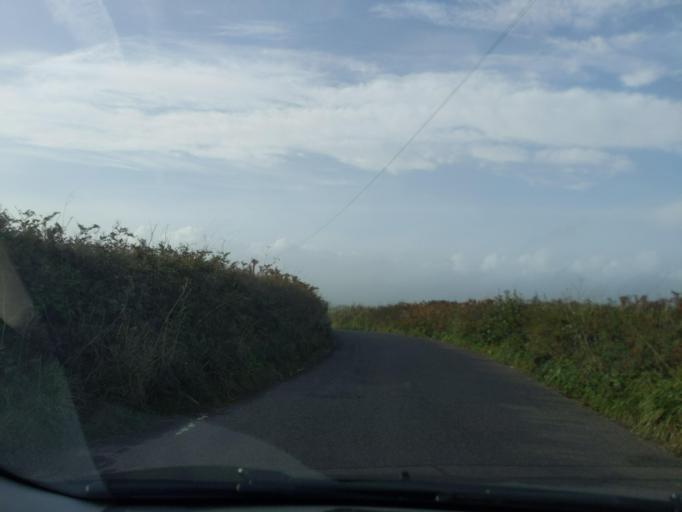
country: GB
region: England
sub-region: Cornwall
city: Pillaton
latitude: 50.3636
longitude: -4.3441
